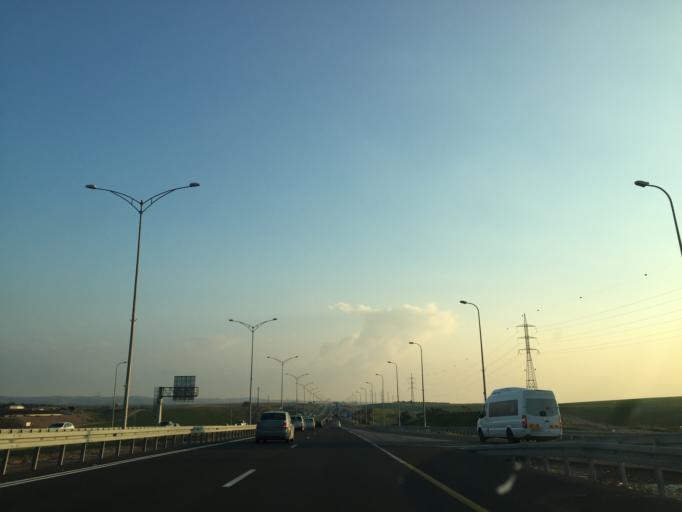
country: IL
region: Southern District
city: Lehavim
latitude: 31.4210
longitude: 34.7853
